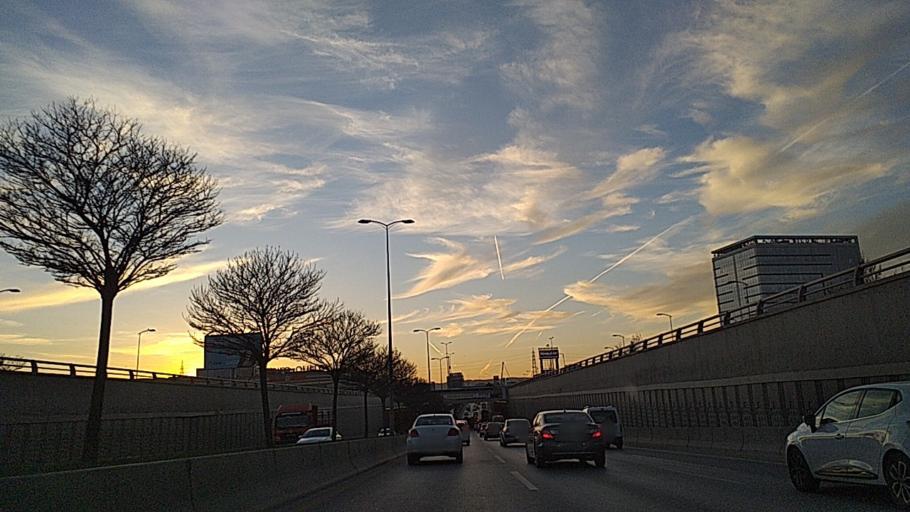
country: TR
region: Ankara
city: Etimesgut
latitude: 39.9653
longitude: 32.6383
